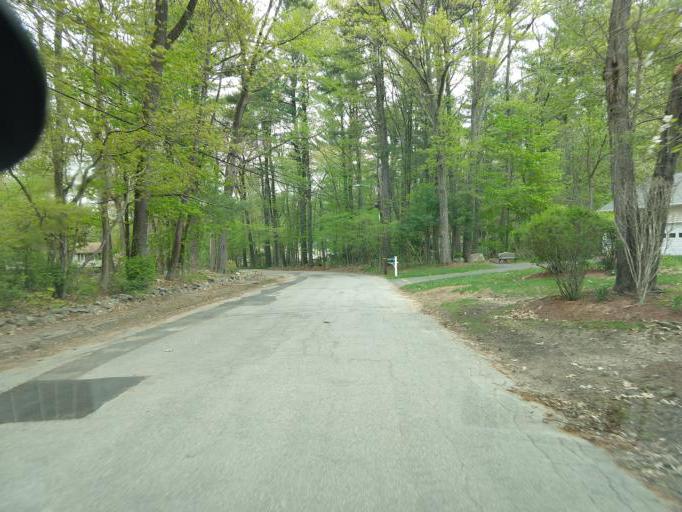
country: US
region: Massachusetts
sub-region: Middlesex County
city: Bedford
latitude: 42.5100
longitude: -71.2832
